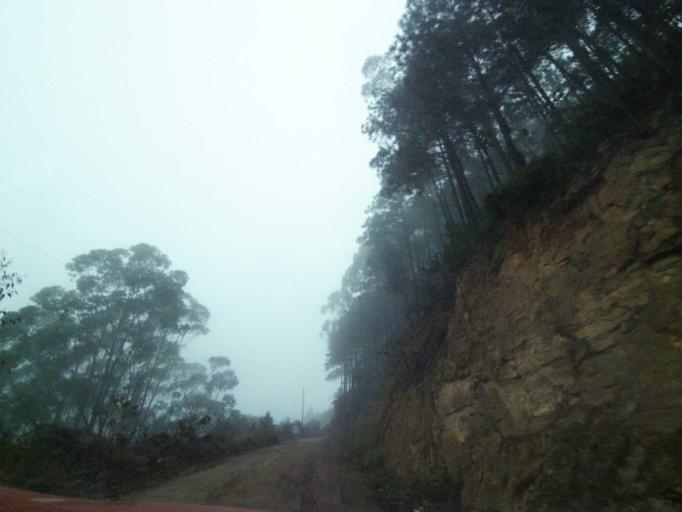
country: BR
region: Santa Catarina
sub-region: Anitapolis
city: Anitapolis
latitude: -27.9096
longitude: -49.1183
